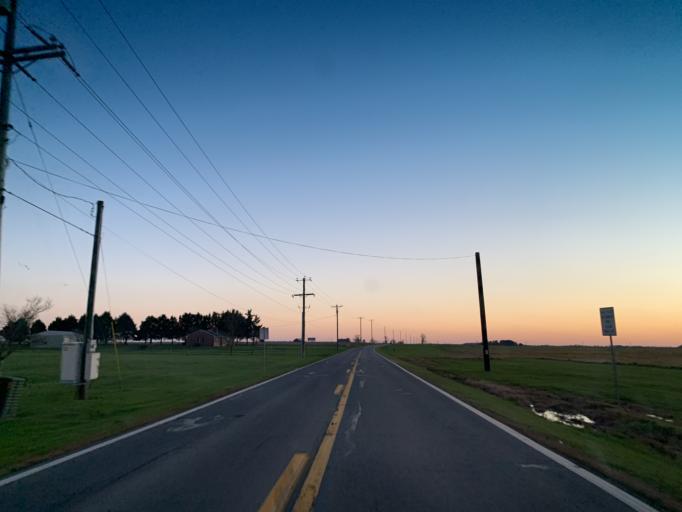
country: US
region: Delaware
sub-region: New Castle County
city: Middletown
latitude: 39.4225
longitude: -75.7414
